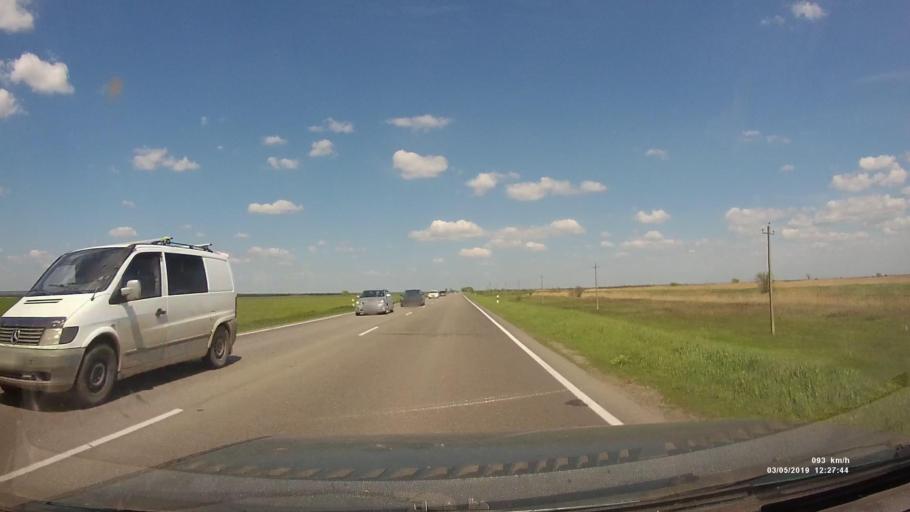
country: RU
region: Rostov
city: Semikarakorsk
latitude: 47.4630
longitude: 40.7227
